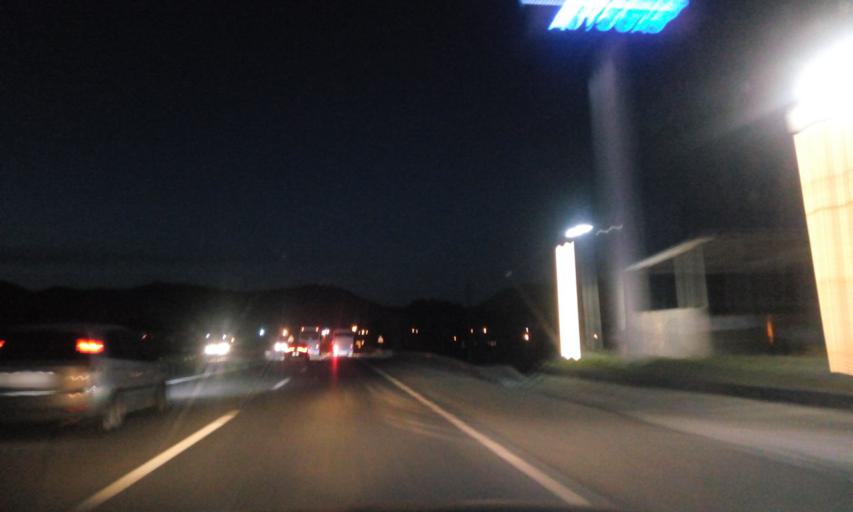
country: TR
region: Sakarya
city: Dogancay
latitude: 40.6777
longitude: 30.3634
